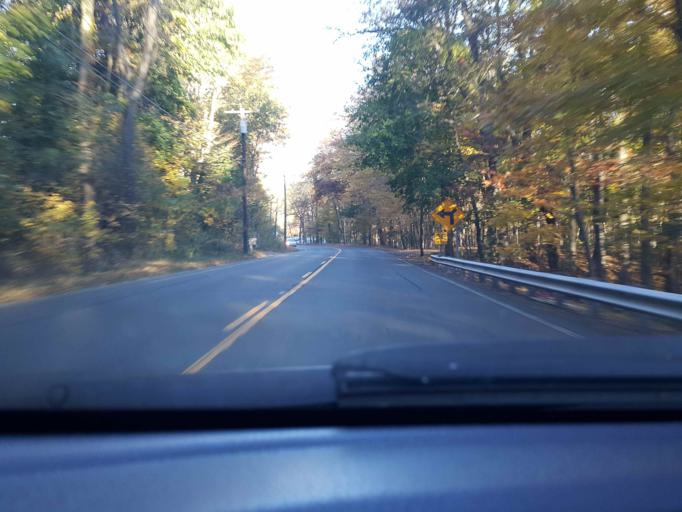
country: US
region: Connecticut
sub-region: New Haven County
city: Woodbridge
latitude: 41.3858
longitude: -73.0181
